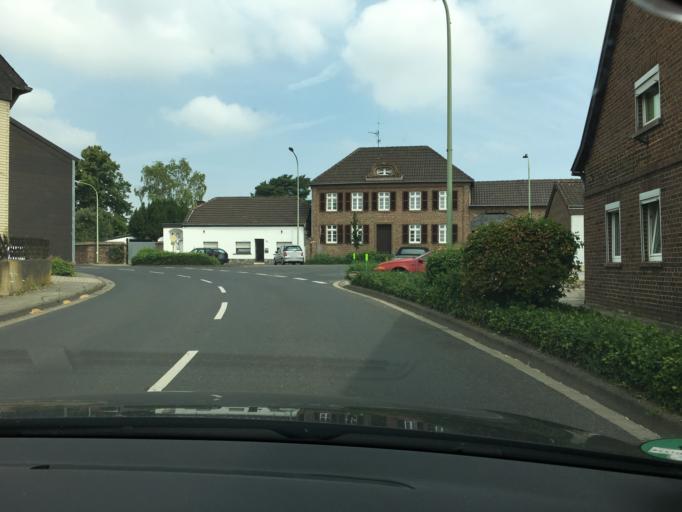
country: DE
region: North Rhine-Westphalia
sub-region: Regierungsbezirk Koln
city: Merzenich
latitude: 50.8392
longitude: 6.5804
